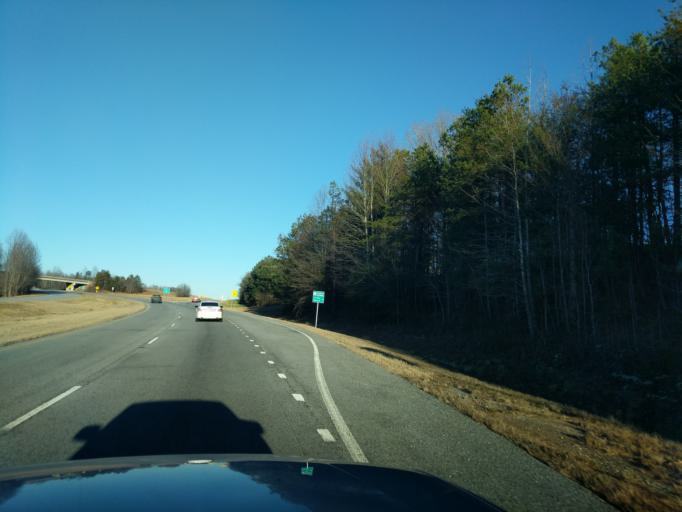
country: US
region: Georgia
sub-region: Habersham County
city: Clarkesville
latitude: 34.5908
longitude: -83.4448
